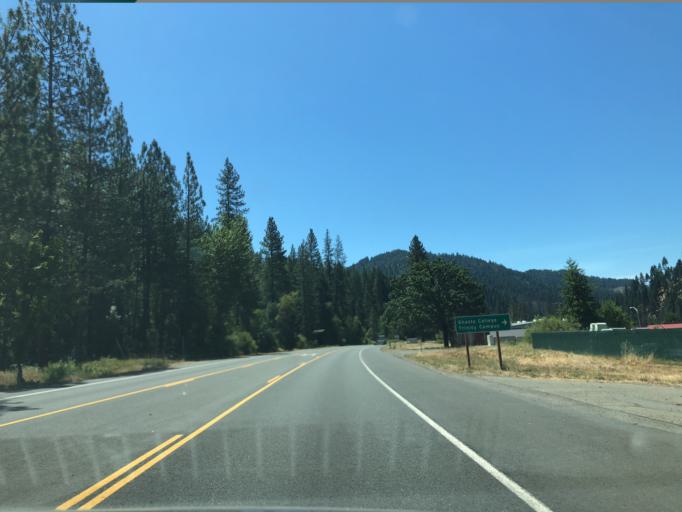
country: US
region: California
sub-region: Trinity County
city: Weaverville
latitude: 40.7129
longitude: -122.9247
